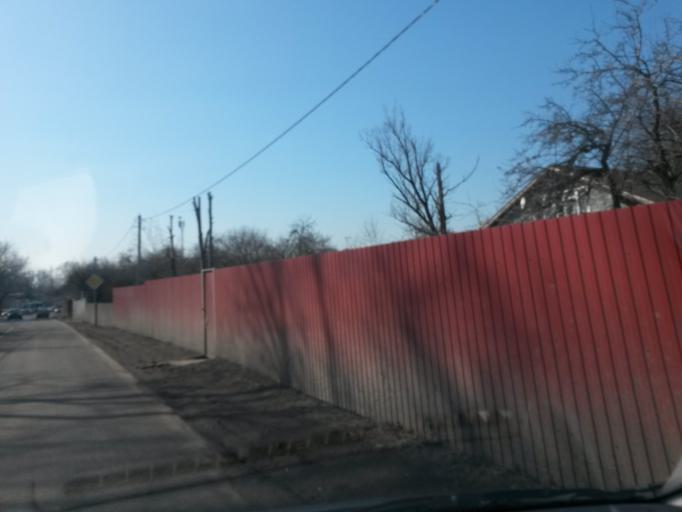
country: RU
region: Moskovskaya
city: Shcherbinka
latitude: 55.5430
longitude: 37.5751
